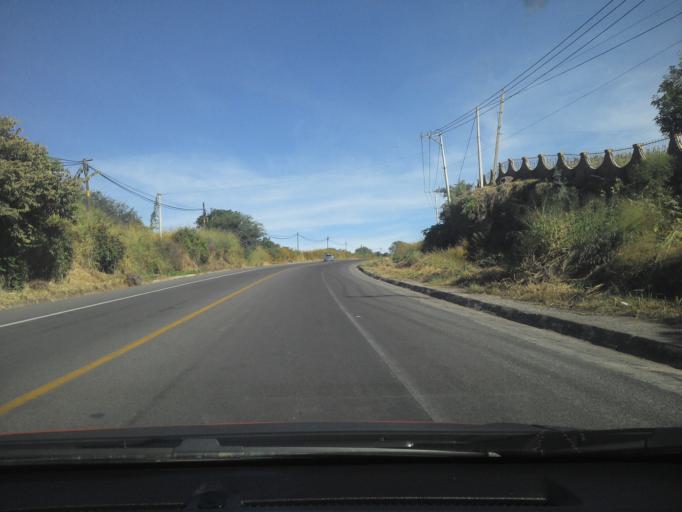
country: MX
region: Jalisco
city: Teuchitlan
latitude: 20.6802
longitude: -103.8426
